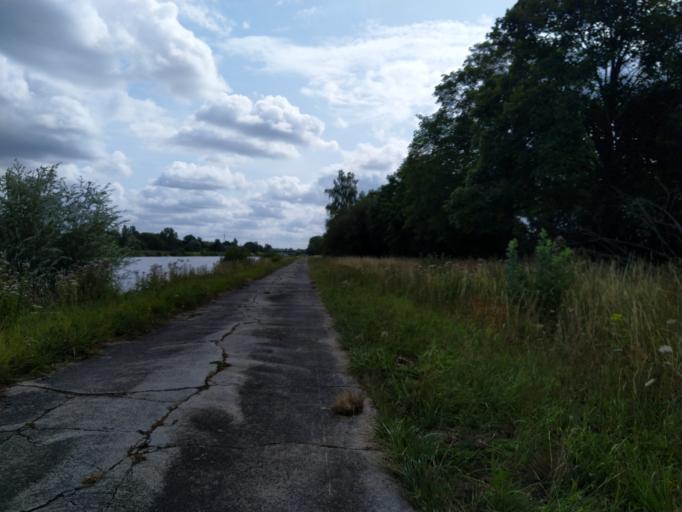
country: BE
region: Wallonia
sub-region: Province du Hainaut
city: Boussu
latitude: 50.4752
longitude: 3.7545
